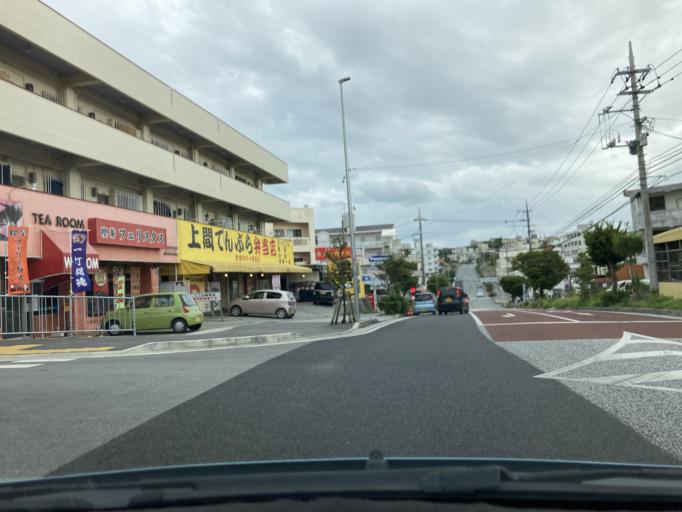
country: JP
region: Okinawa
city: Ginowan
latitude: 26.2539
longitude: 127.7568
